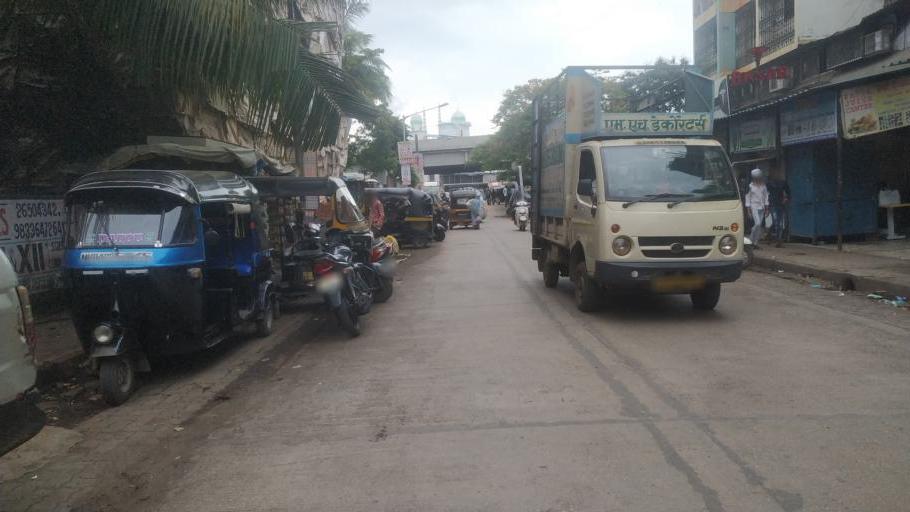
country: IN
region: Maharashtra
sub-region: Mumbai Suburban
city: Mumbai
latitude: 19.0706
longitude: 72.8845
